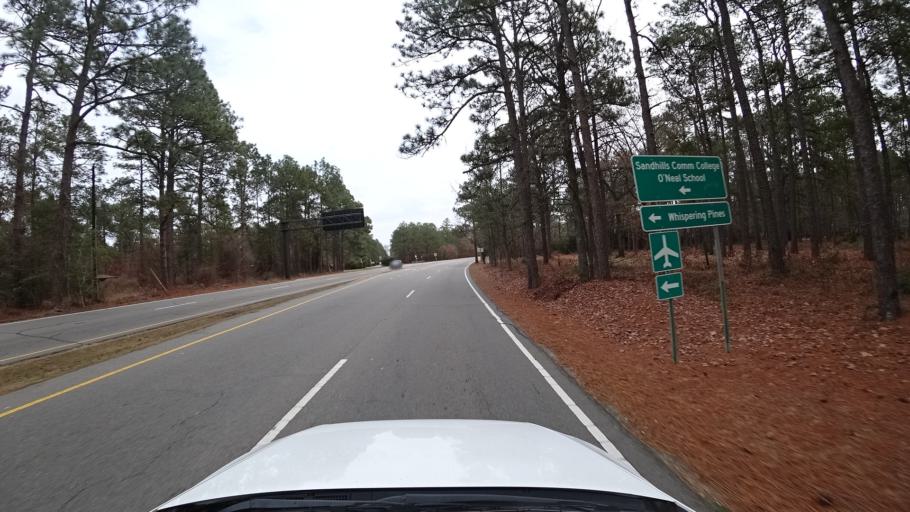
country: US
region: North Carolina
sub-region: Moore County
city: Pinehurst
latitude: 35.2028
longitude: -79.4473
